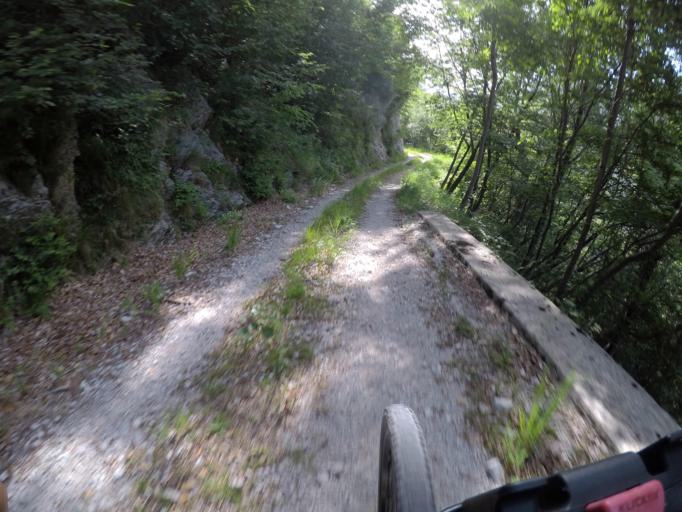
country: IT
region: Friuli Venezia Giulia
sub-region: Provincia di Udine
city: Resiutta
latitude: 46.3256
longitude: 13.2195
